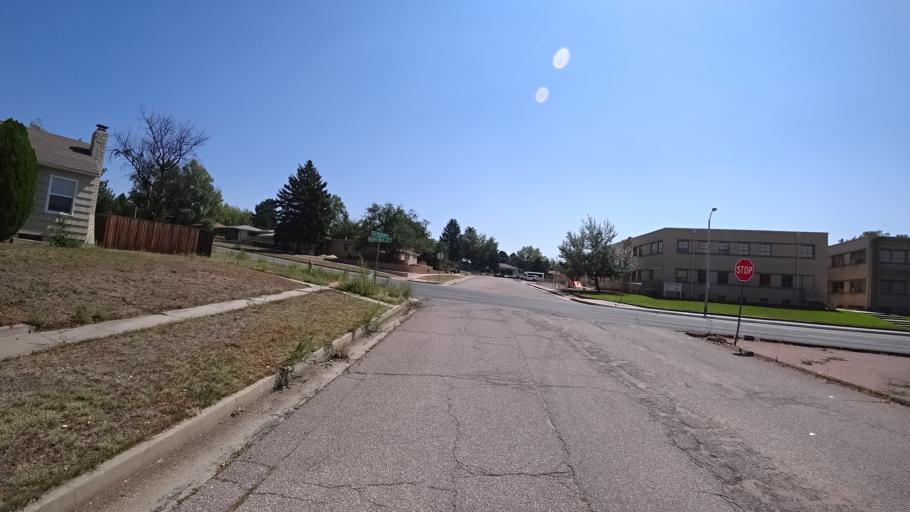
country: US
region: Colorado
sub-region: El Paso County
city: Colorado Springs
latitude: 38.8508
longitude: -104.7997
